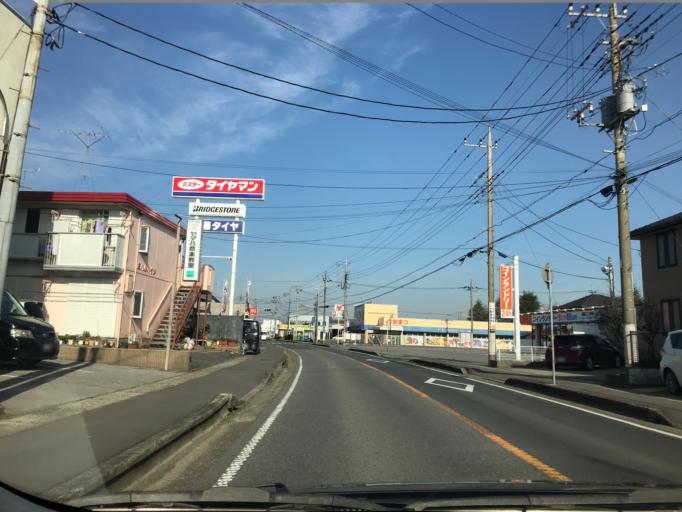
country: JP
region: Ibaraki
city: Mitsukaido
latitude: 36.0308
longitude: 139.9912
